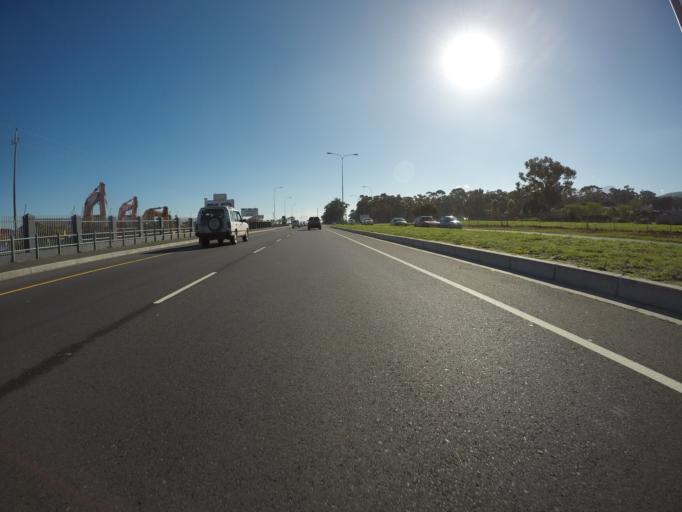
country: ZA
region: Western Cape
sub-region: Overberg District Municipality
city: Grabouw
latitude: -34.1186
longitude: 18.8782
